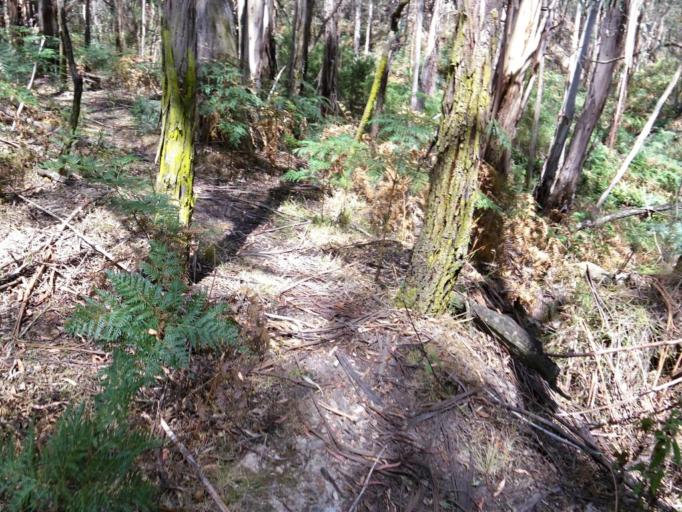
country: AU
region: Victoria
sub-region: Melton
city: Melton West
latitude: -37.4913
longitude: 144.5358
